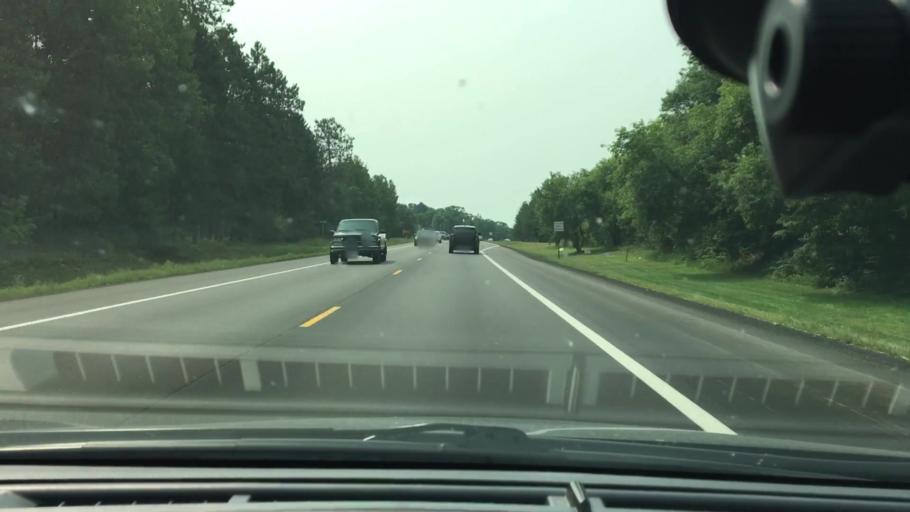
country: US
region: Minnesota
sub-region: Crow Wing County
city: Brainerd
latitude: 46.4400
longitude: -94.1716
